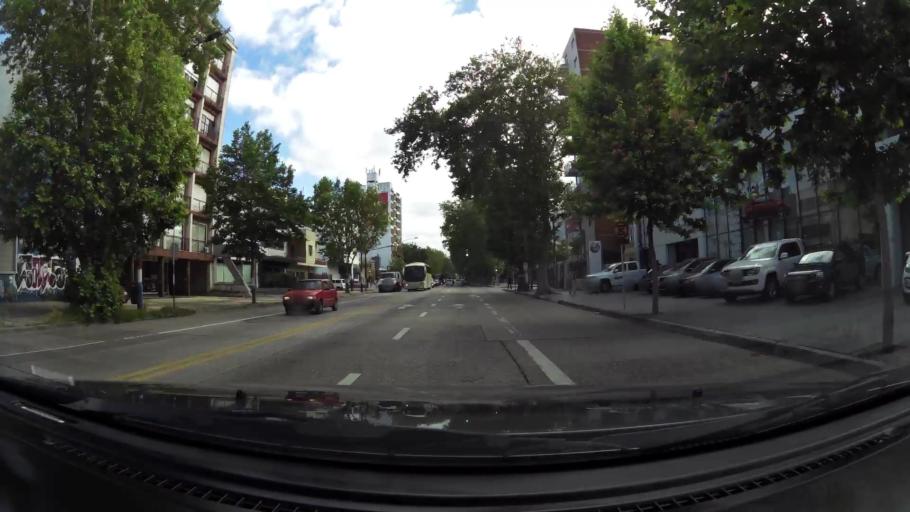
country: UY
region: Montevideo
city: Montevideo
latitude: -34.8877
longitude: -56.1587
